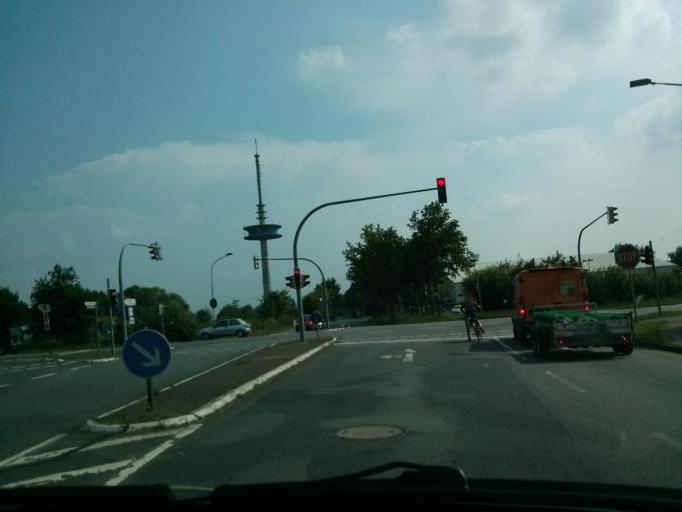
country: DE
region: Lower Saxony
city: Schiffdorf
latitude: 53.5266
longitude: 8.6473
